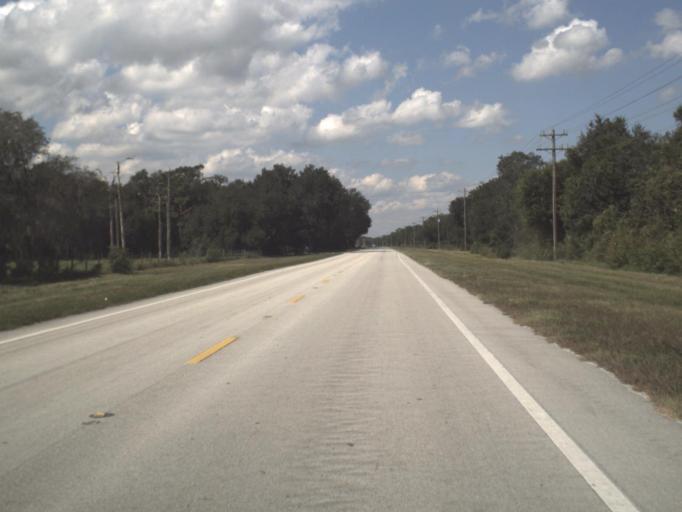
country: US
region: Florida
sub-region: Okeechobee County
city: Okeechobee
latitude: 27.3872
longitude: -81.0146
